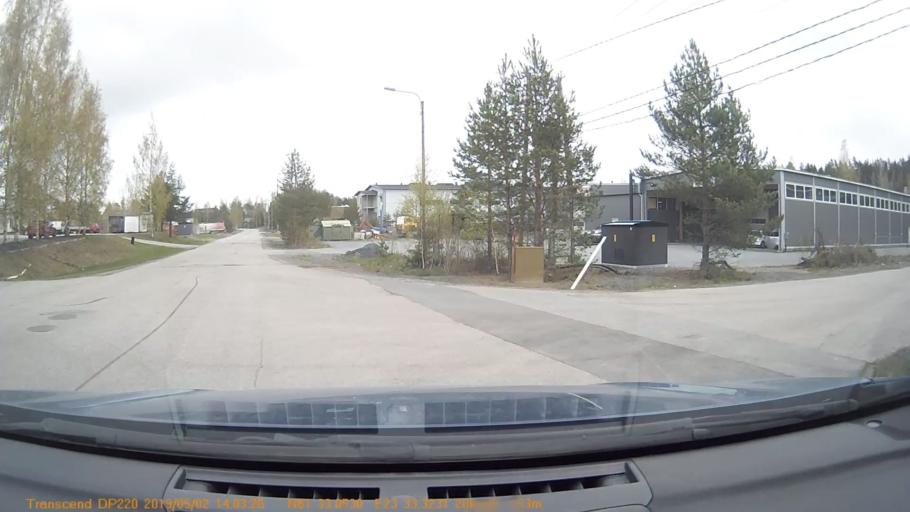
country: FI
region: Pirkanmaa
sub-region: Tampere
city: Yloejaervi
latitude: 61.5510
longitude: 23.5552
